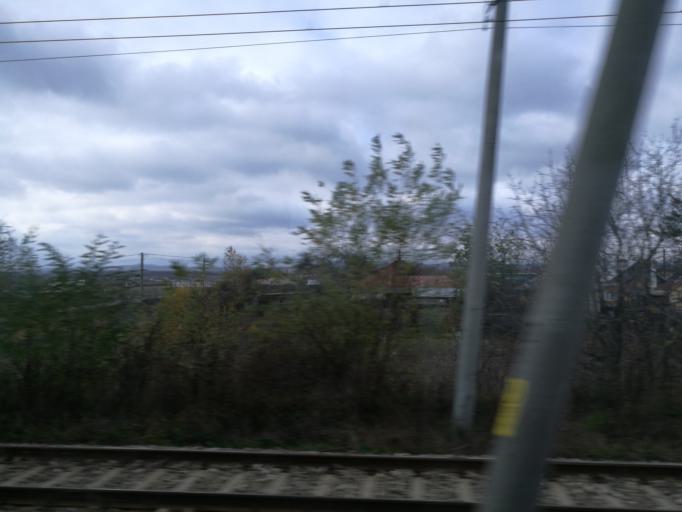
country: RO
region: Bacau
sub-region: Comuna Sascut
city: Sascut
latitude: 46.2149
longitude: 27.1052
